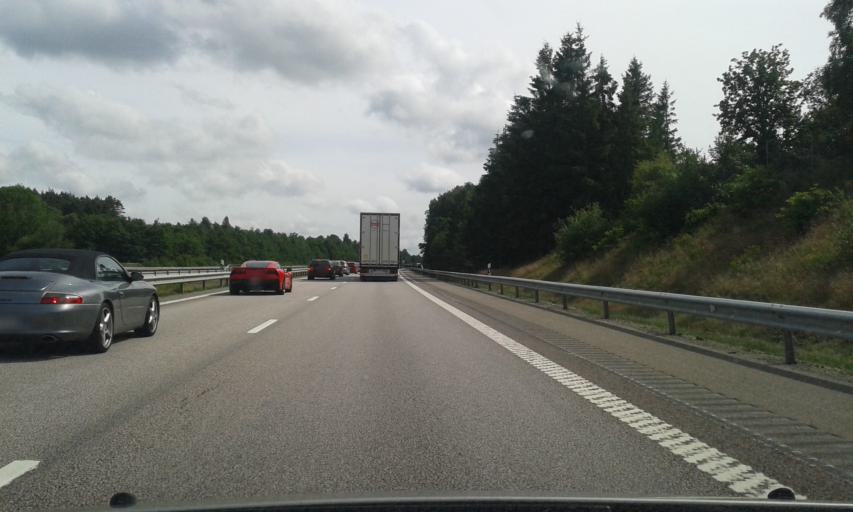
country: SE
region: Halland
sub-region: Kungsbacka Kommun
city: Frillesas
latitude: 57.3604
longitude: 12.2079
